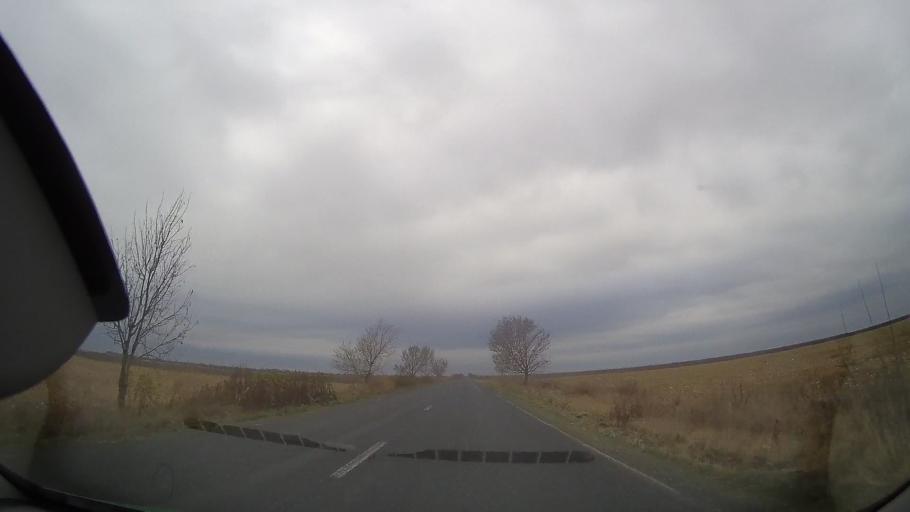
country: RO
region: Buzau
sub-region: Comuna Padina
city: Padina
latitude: 44.7903
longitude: 27.1440
